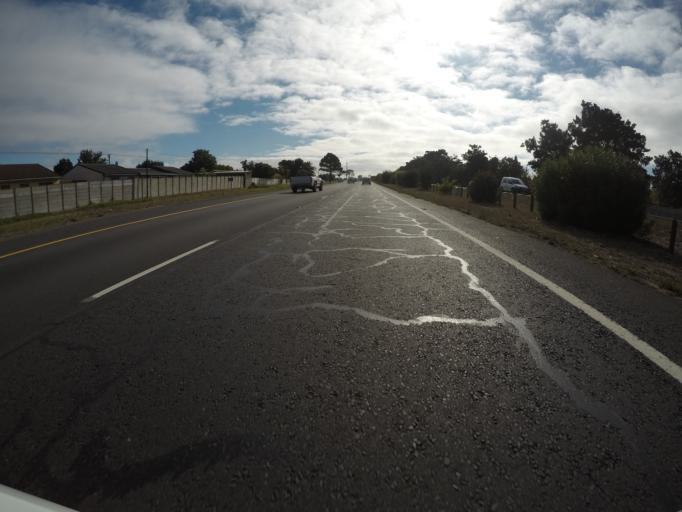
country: ZA
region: Western Cape
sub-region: City of Cape Town
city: Kraaifontein
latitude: -33.8410
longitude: 18.7215
